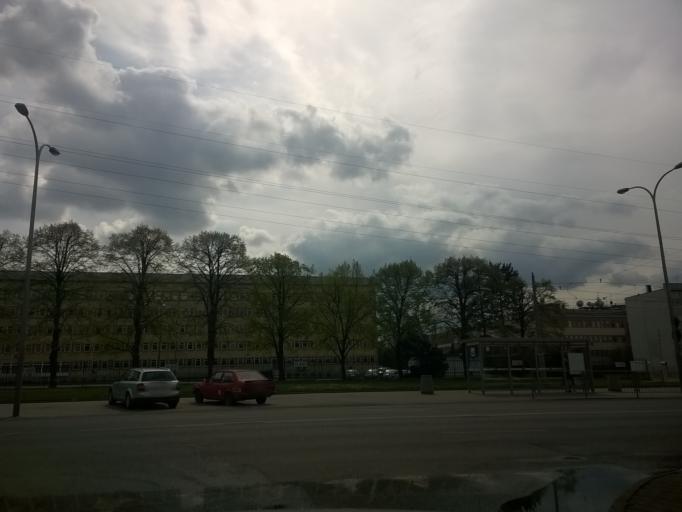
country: PL
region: Masovian Voivodeship
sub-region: Warszawa
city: Mokotow
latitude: 52.1891
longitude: 21.0125
